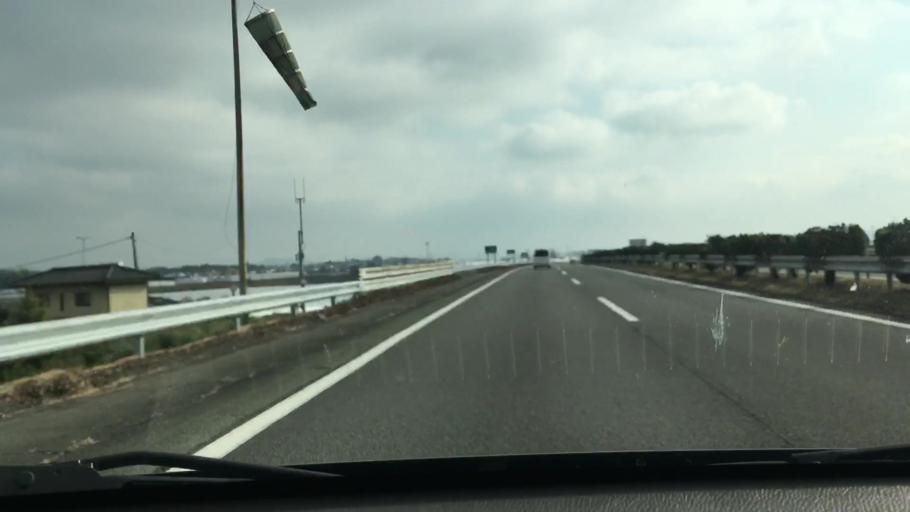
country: JP
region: Kumamoto
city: Ueki
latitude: 32.8881
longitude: 130.7235
